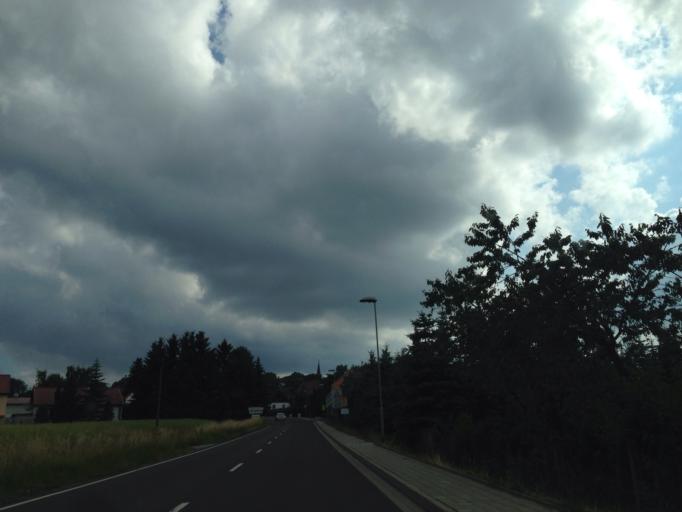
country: DE
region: Thuringia
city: Schwarza
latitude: 50.8143
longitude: 11.3369
